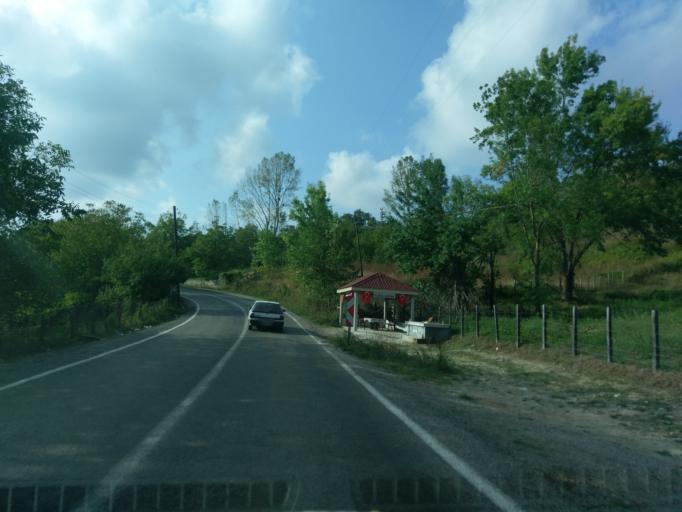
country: TR
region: Sinop
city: Helaldi
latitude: 41.9163
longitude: 34.4191
